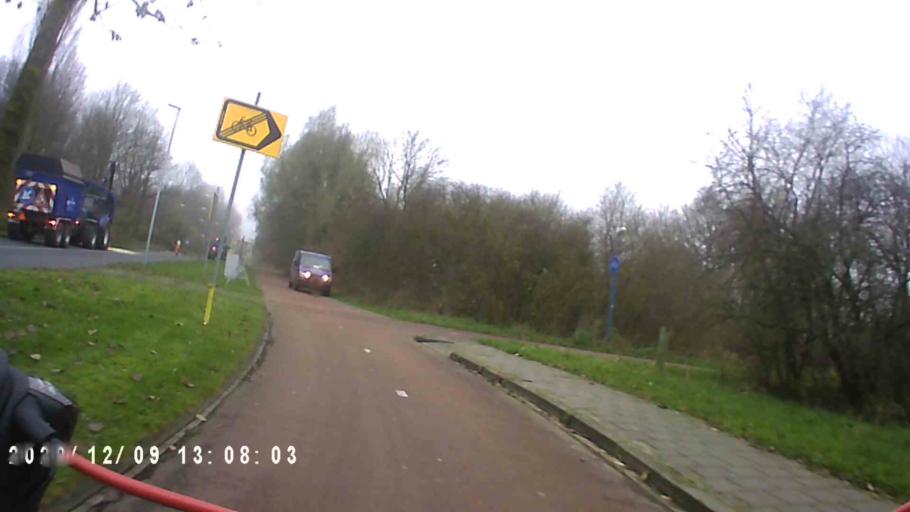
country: NL
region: Groningen
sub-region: Gemeente Groningen
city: Oosterpark
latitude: 53.2403
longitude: 6.6142
